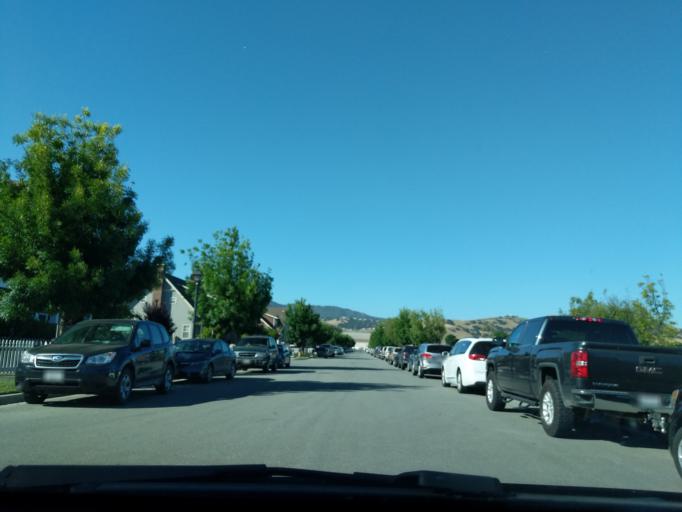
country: US
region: California
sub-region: Monterey County
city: Salinas
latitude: 36.6274
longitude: -121.6488
